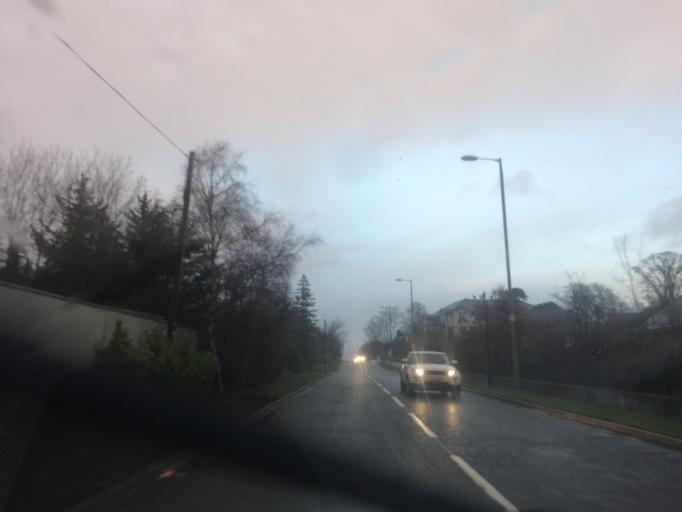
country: GB
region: Scotland
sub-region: East Renfrewshire
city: Newton Mearns
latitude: 55.7887
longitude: -4.3395
